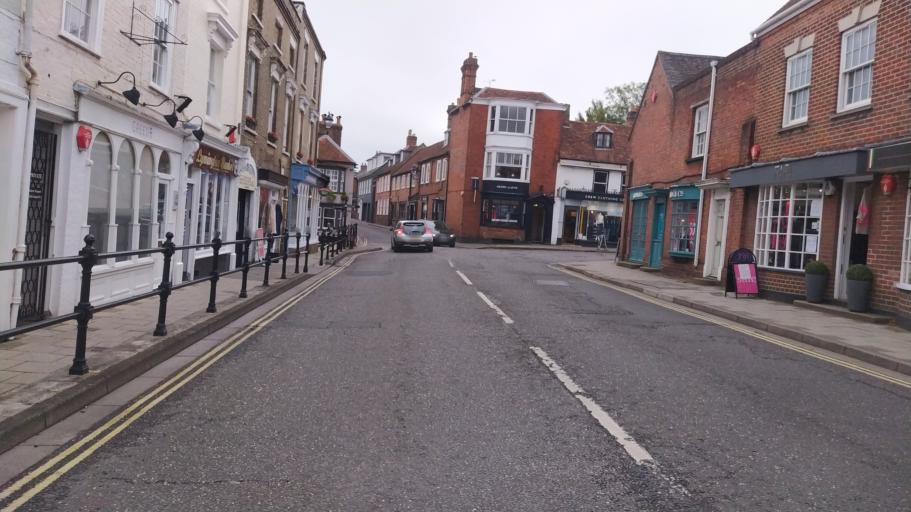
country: GB
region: England
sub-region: Hampshire
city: Lymington
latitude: 50.7594
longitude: -1.5384
